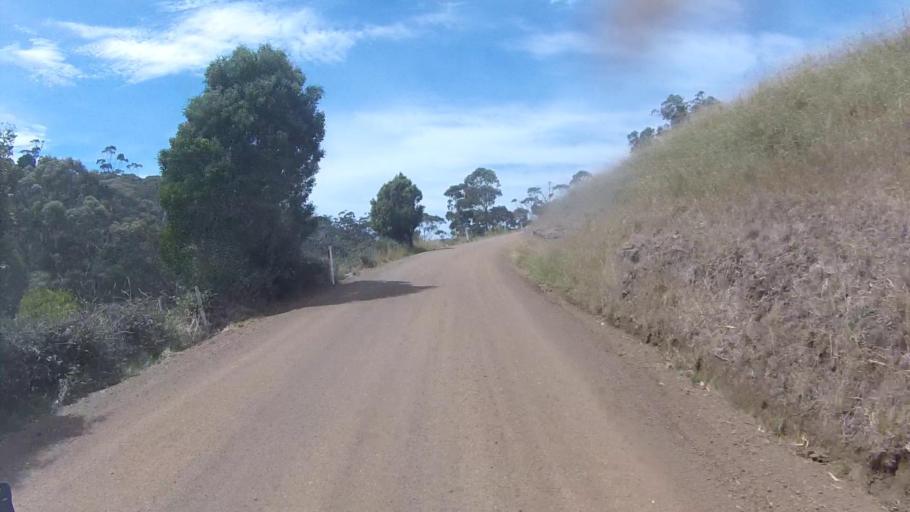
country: AU
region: Tasmania
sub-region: Sorell
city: Sorell
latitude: -42.7876
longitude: 147.8420
